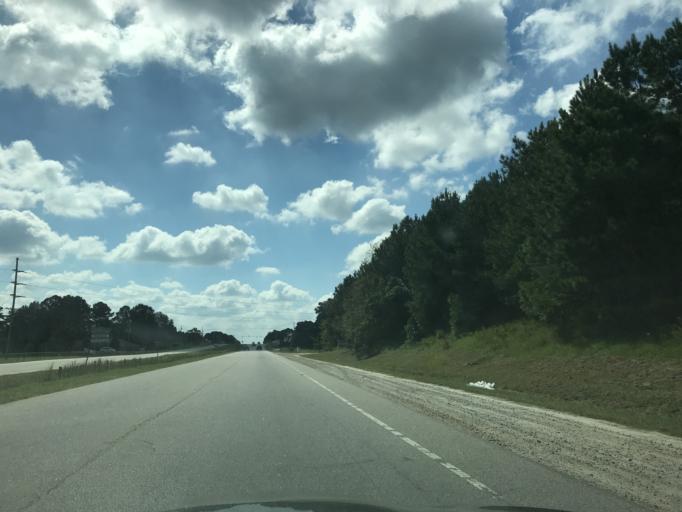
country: US
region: North Carolina
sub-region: Franklin County
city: Franklinton
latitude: 36.1016
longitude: -78.4666
